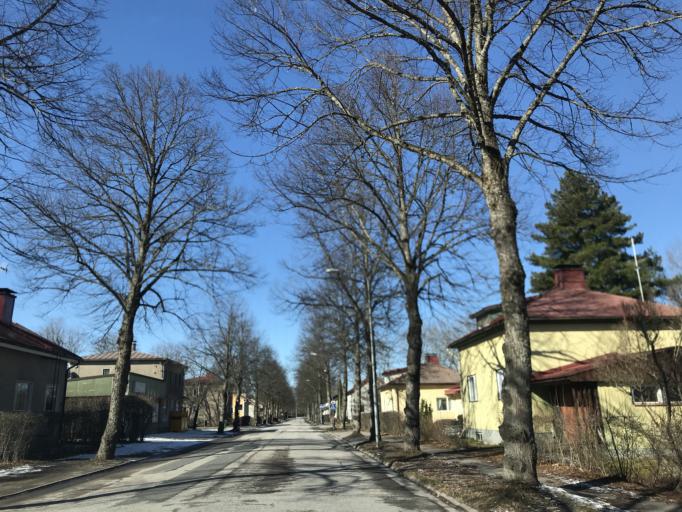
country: FI
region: Uusimaa
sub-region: Raaseporin
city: Karis
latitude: 60.0751
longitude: 23.6876
